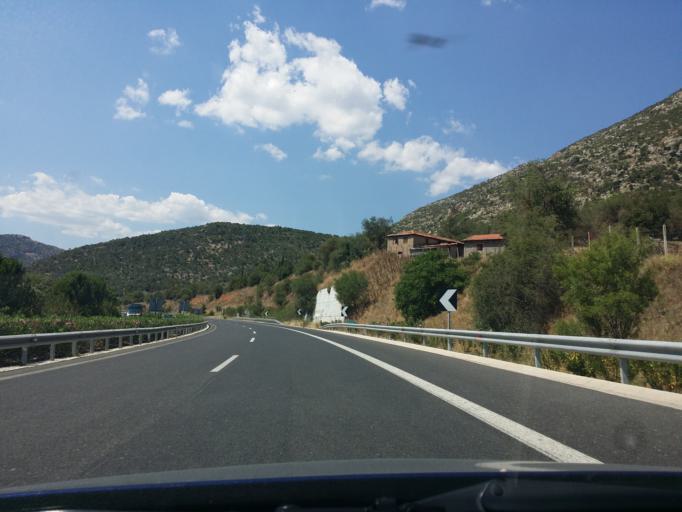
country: GR
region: Peloponnese
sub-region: Nomos Arkadias
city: Tripoli
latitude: 37.6307
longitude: 22.4680
